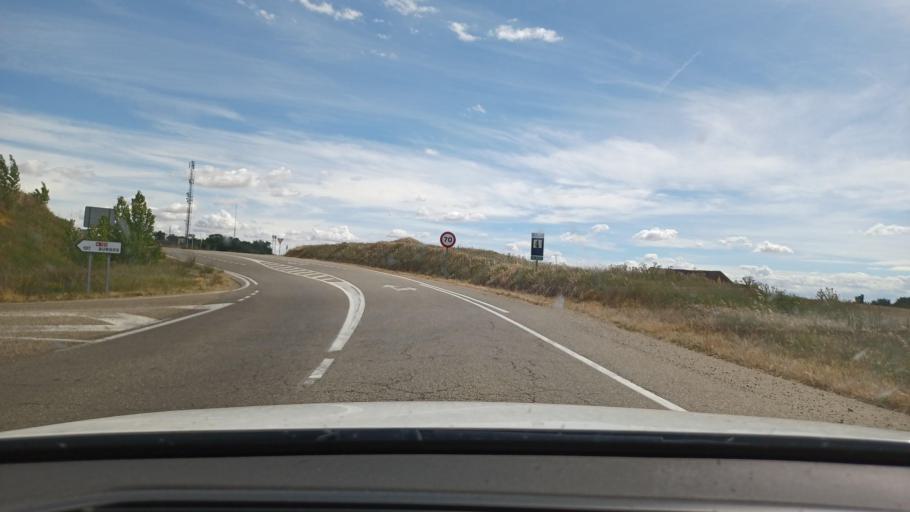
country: ES
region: Castille and Leon
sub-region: Provincia de Leon
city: Sahagun
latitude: 42.3778
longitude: -5.0274
